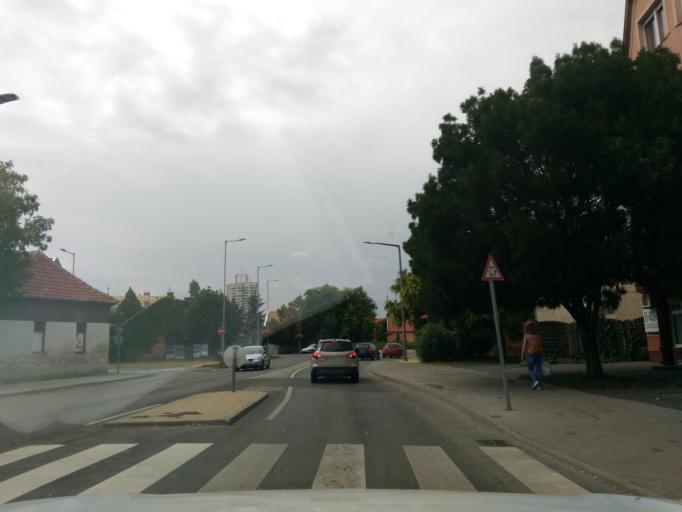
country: HU
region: Jasz-Nagykun-Szolnok
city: Szolnok
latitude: 47.1786
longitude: 20.1865
